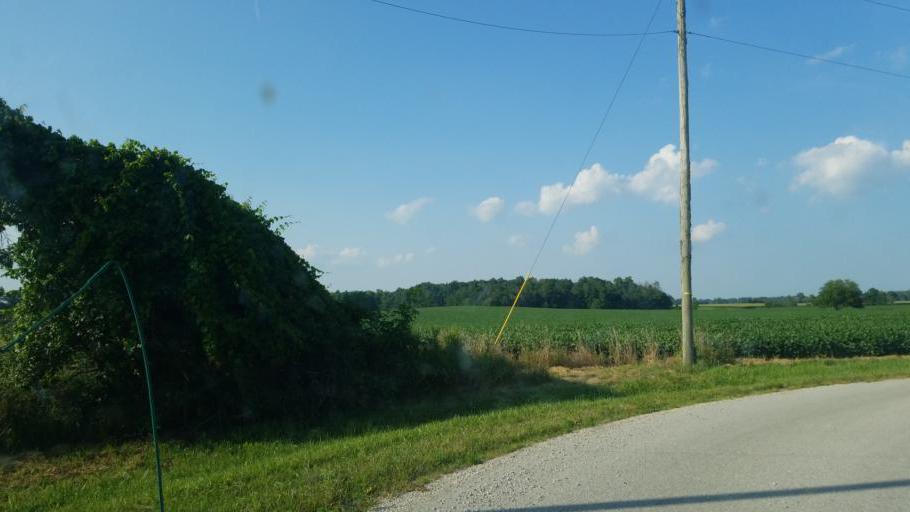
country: US
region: Ohio
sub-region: Crawford County
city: Bucyrus
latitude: 40.8445
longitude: -82.9782
